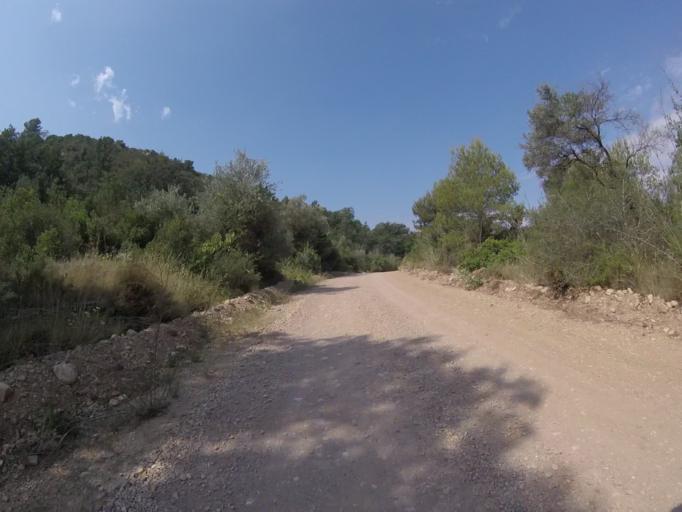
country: ES
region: Valencia
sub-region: Provincia de Castello
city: Cuevas de Vinroma
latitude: 40.3036
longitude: 0.1698
